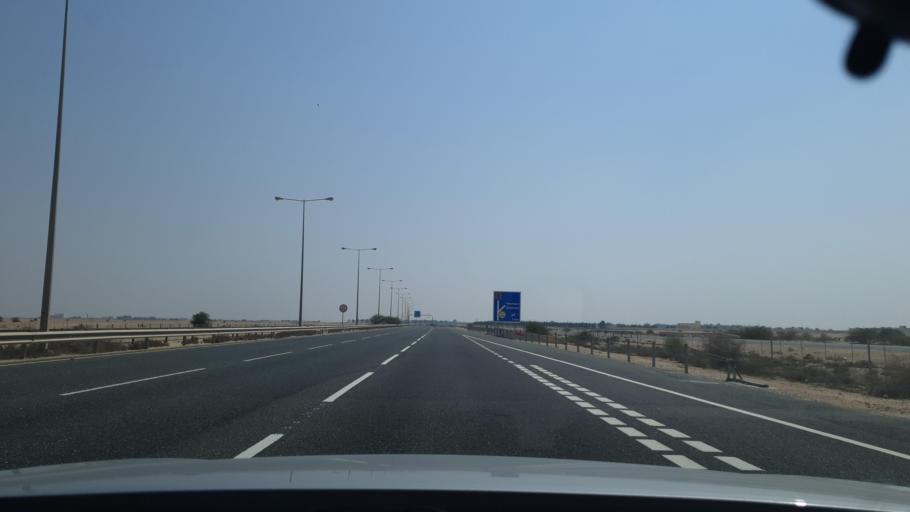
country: QA
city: Al Ghuwayriyah
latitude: 25.7962
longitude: 51.3864
